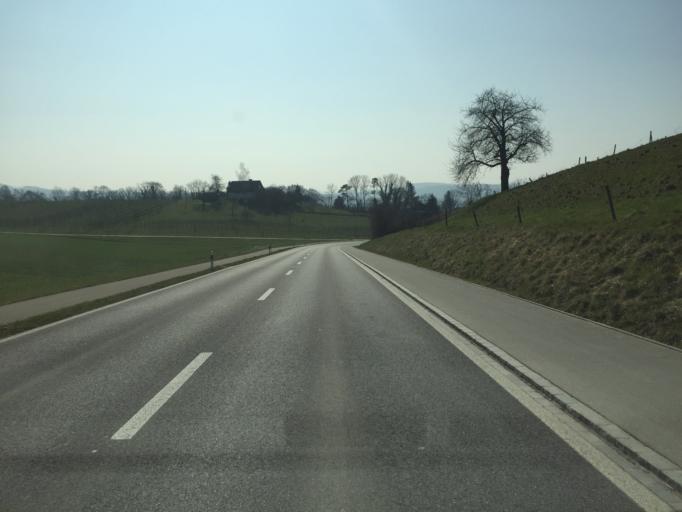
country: CH
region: Thurgau
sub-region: Frauenfeld District
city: Huttwilen
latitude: 47.5851
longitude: 8.8821
